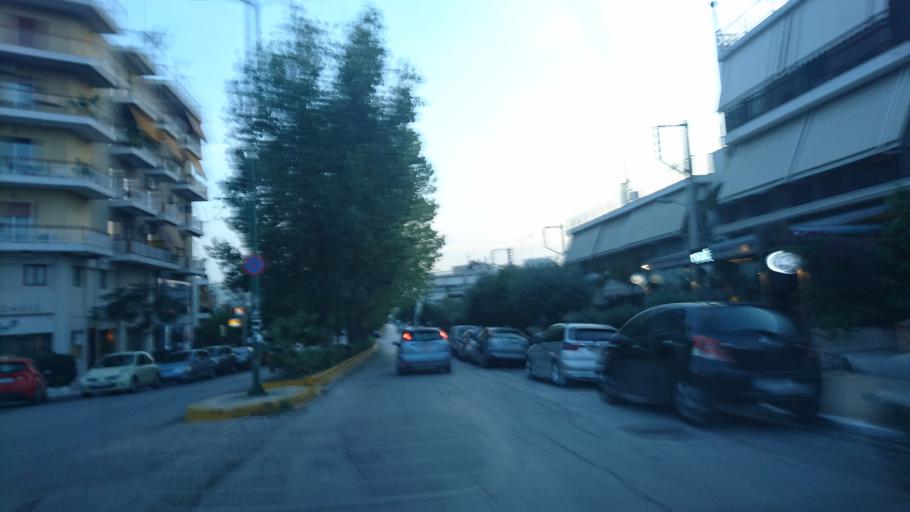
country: GR
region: Attica
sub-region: Nomarchia Athinas
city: Ilioupoli
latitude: 37.9311
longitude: 23.7555
